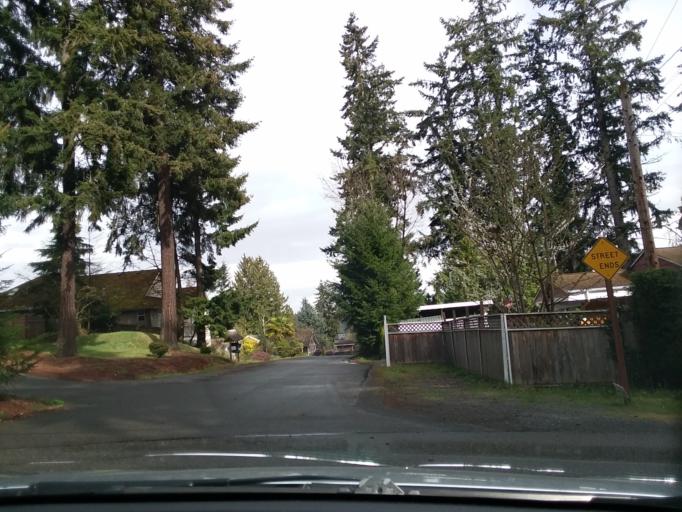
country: US
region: Washington
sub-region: Snohomish County
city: Esperance
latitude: 47.7832
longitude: -122.3382
